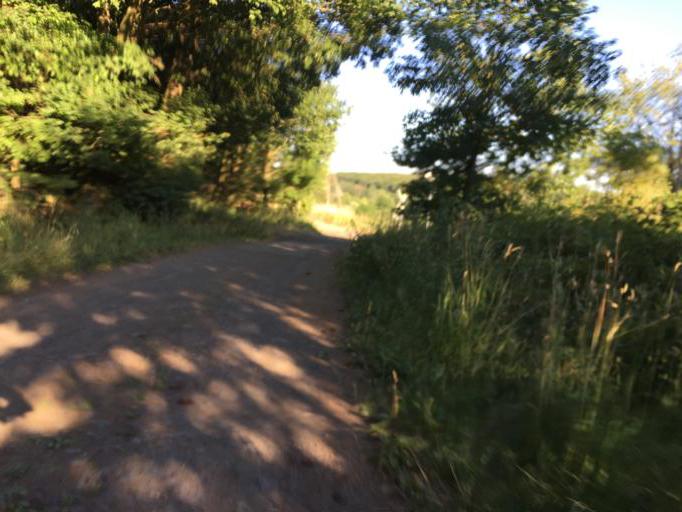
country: DE
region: Rheinland-Pfalz
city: Berod bei Wallmerod
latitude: 50.4900
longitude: 7.9334
